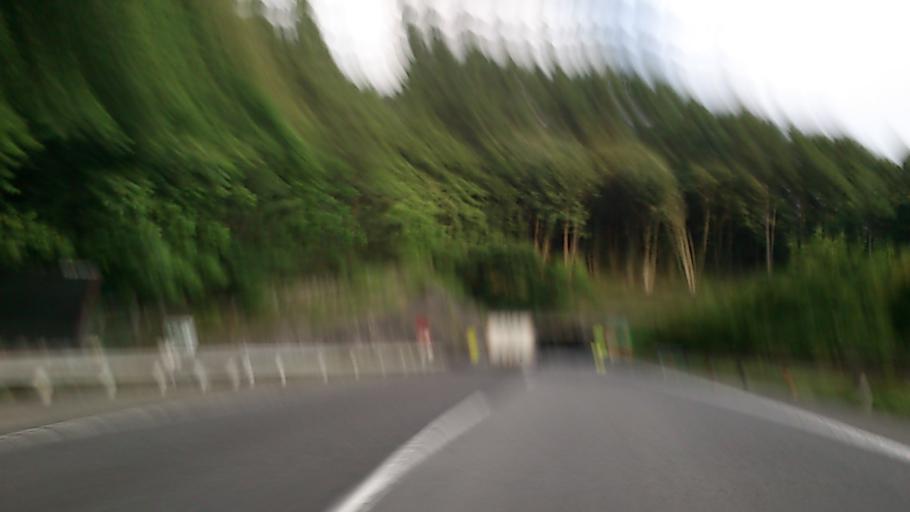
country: JP
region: Nagano
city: Tatsuno
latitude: 36.0019
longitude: 138.0084
